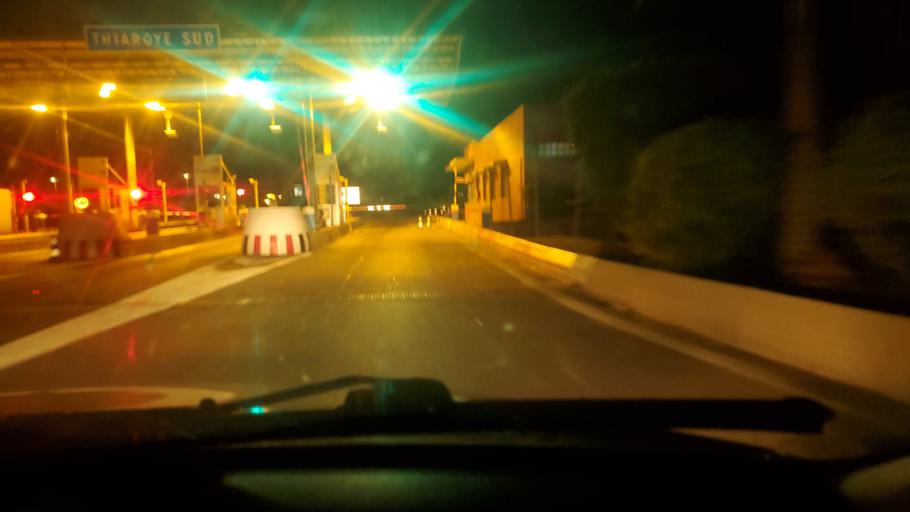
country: SN
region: Dakar
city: Pikine
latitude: 14.7488
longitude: -17.3784
